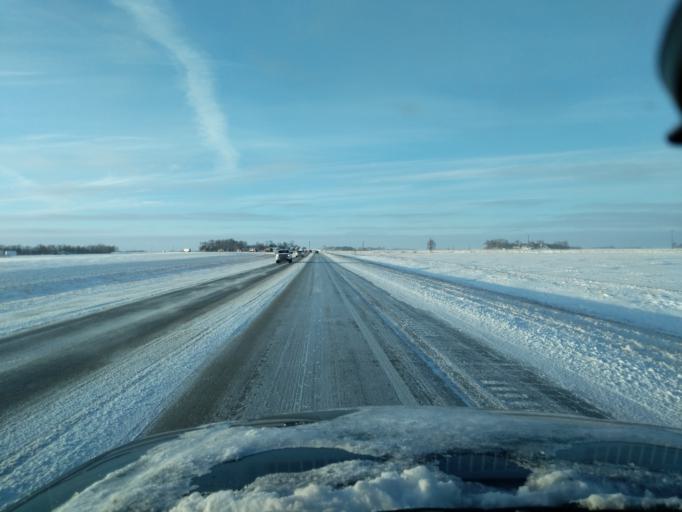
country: US
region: Minnesota
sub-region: Renville County
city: Bird Island
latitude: 44.7703
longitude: -94.9400
